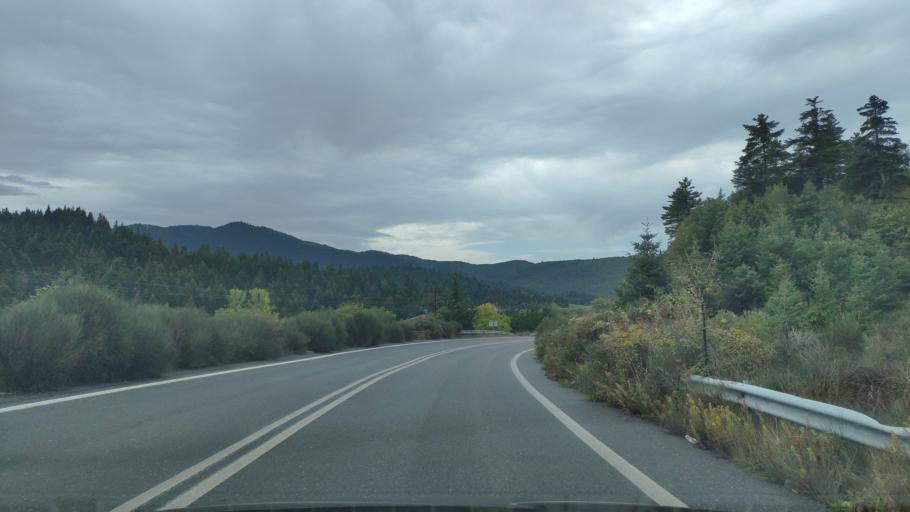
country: GR
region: Peloponnese
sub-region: Nomos Arkadias
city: Dimitsana
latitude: 37.6375
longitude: 22.0907
